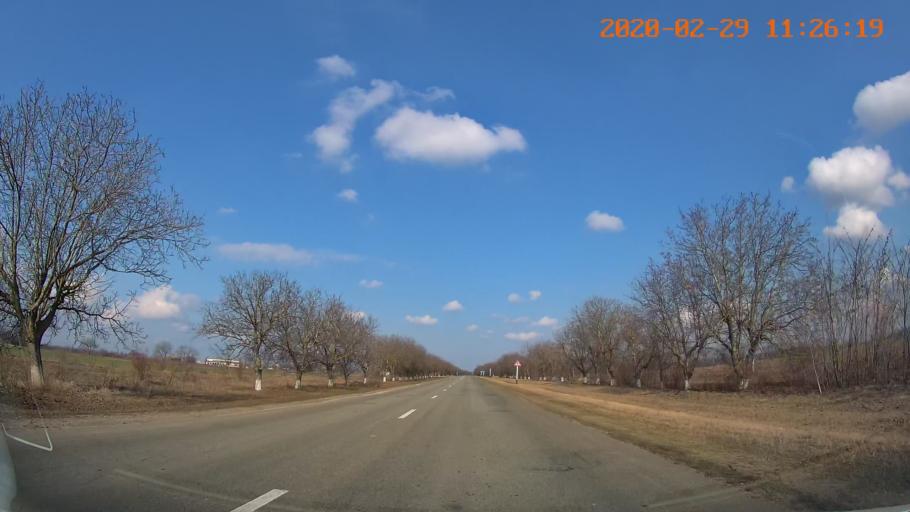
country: MD
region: Telenesti
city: Cocieri
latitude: 47.4515
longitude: 29.1465
